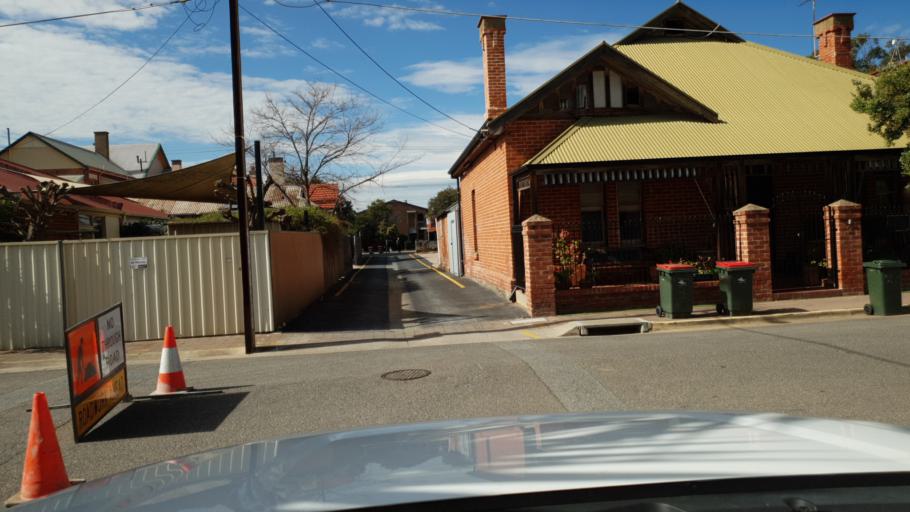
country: AU
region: South Australia
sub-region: Adelaide
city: Glenelg
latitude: -34.9820
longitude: 138.5123
